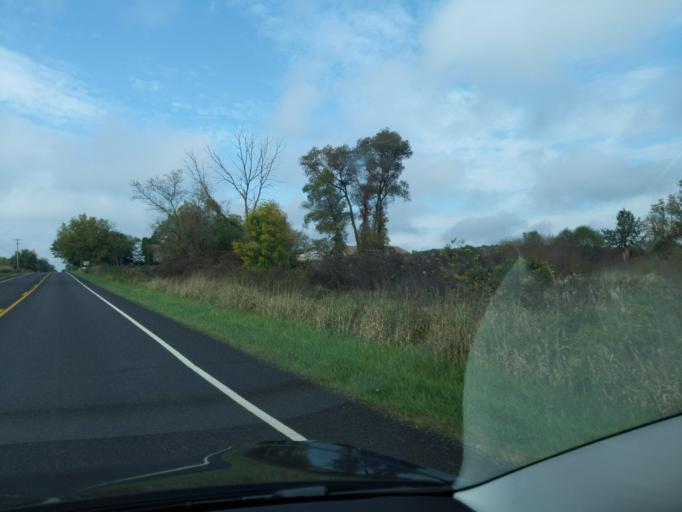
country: US
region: Michigan
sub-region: Eaton County
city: Potterville
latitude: 42.6256
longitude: -84.7101
